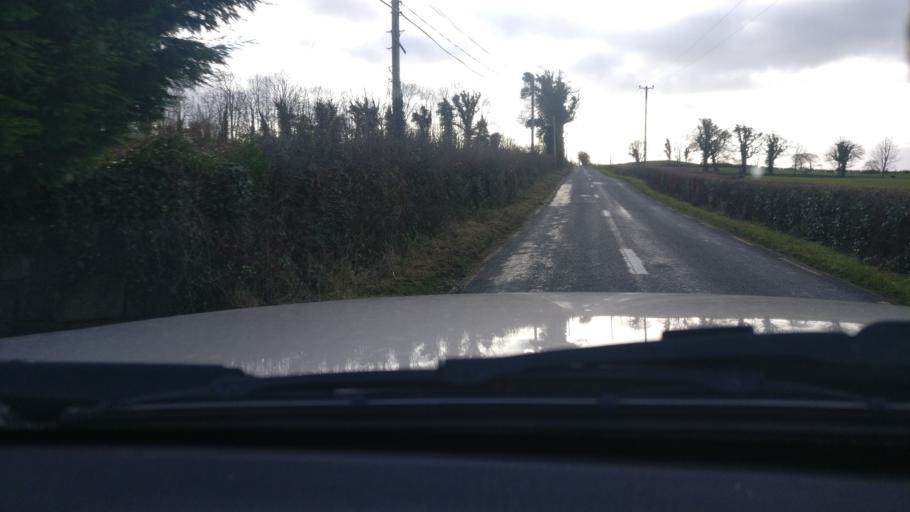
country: IE
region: Connaught
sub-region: County Galway
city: Ballinasloe
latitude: 53.2635
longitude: -8.2545
